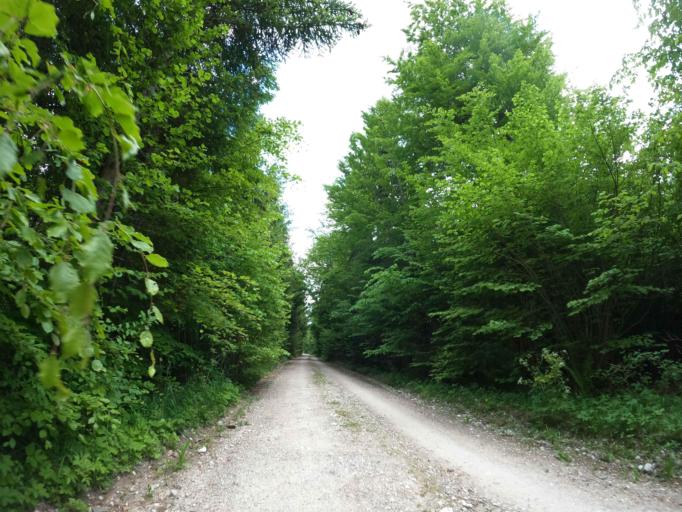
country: DE
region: Bavaria
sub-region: Upper Bavaria
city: Brunnthal
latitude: 47.9745
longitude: 11.7006
